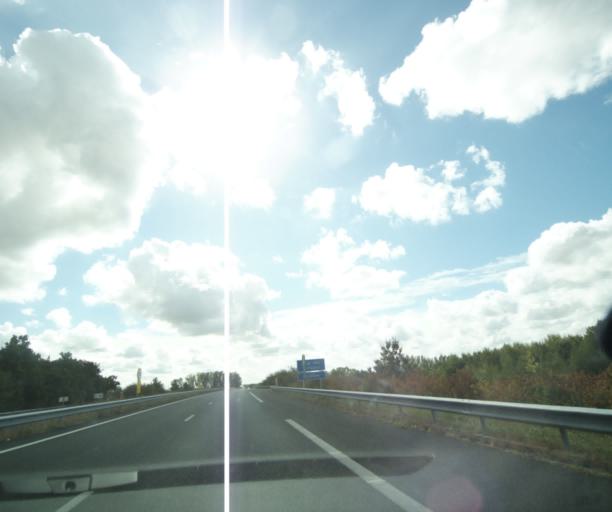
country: FR
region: Poitou-Charentes
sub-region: Departement de la Charente-Maritime
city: Bords
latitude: 45.8872
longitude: -0.7424
